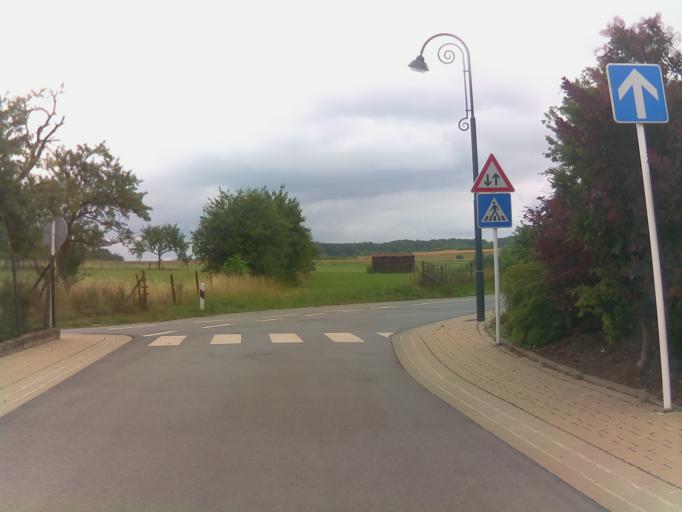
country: LU
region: Grevenmacher
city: Schengen
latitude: 49.4837
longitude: 6.3251
